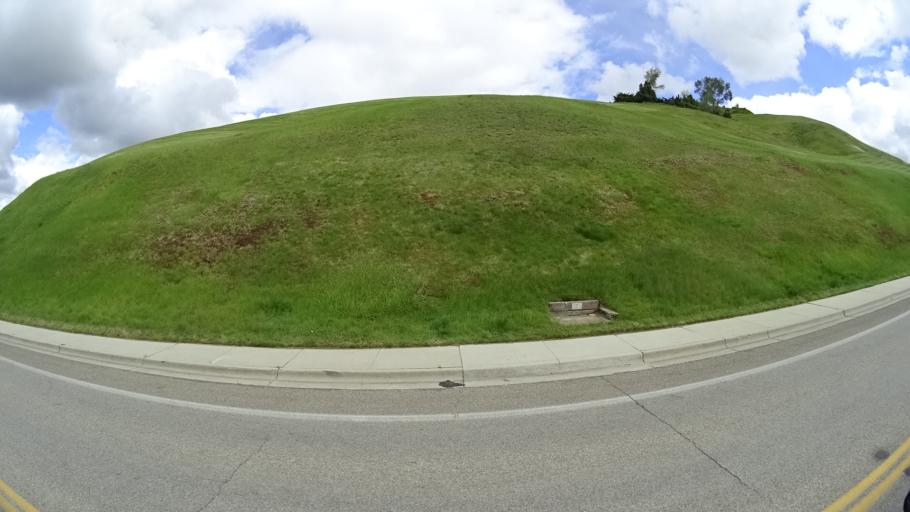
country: US
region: Idaho
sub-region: Ada County
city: Boise
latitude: 43.6500
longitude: -116.1985
